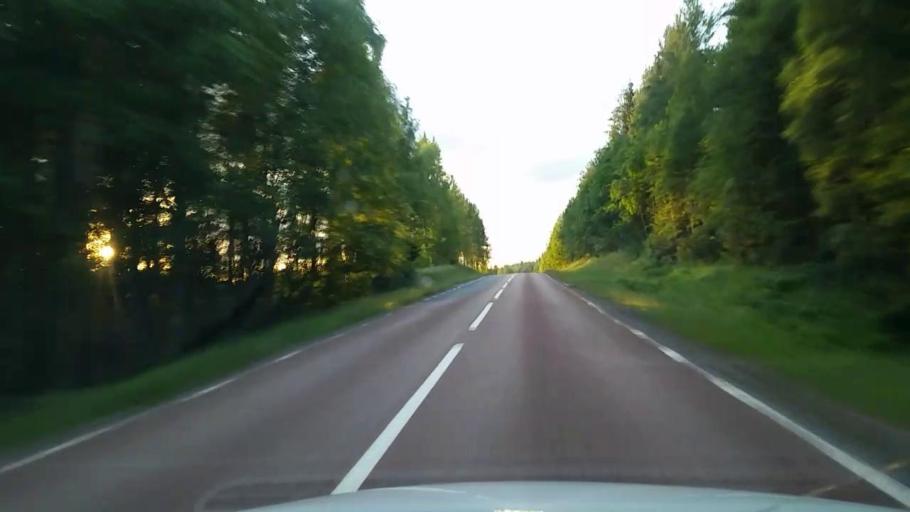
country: SE
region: Gaevleborg
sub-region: Ljusdals Kommun
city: Farila
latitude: 62.1451
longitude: 15.6856
